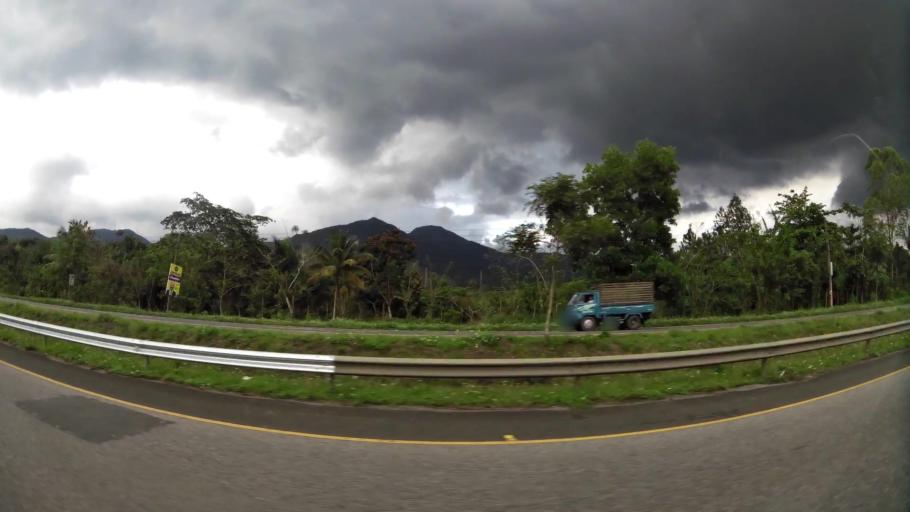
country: DO
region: Monsenor Nouel
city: Juan Adrian
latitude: 18.7596
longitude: -70.2377
